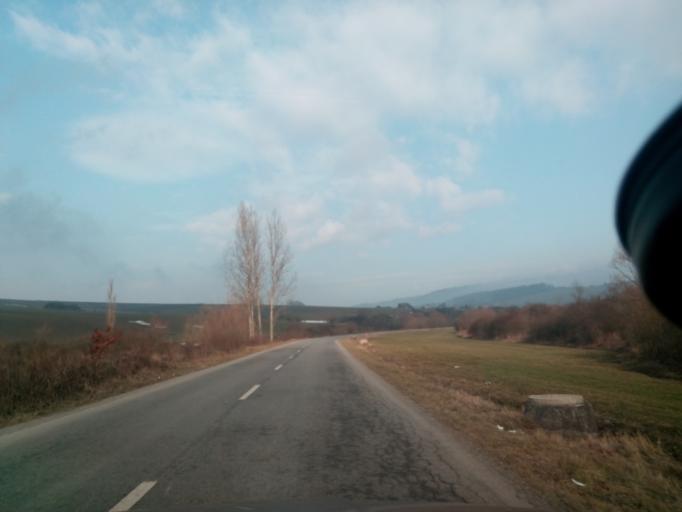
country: SK
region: Presovsky
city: Lipany
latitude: 49.1656
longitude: 20.8709
